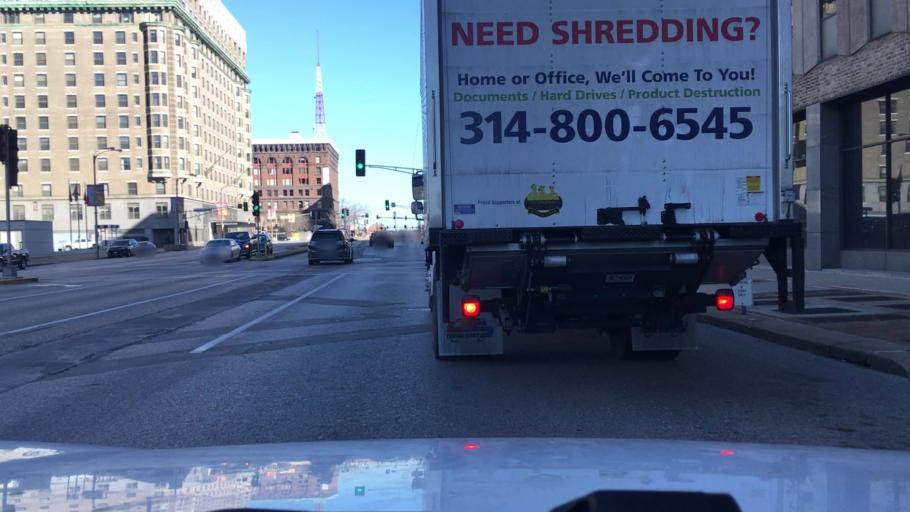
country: US
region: Missouri
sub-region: City of Saint Louis
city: St. Louis
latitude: 38.6295
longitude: -90.1984
